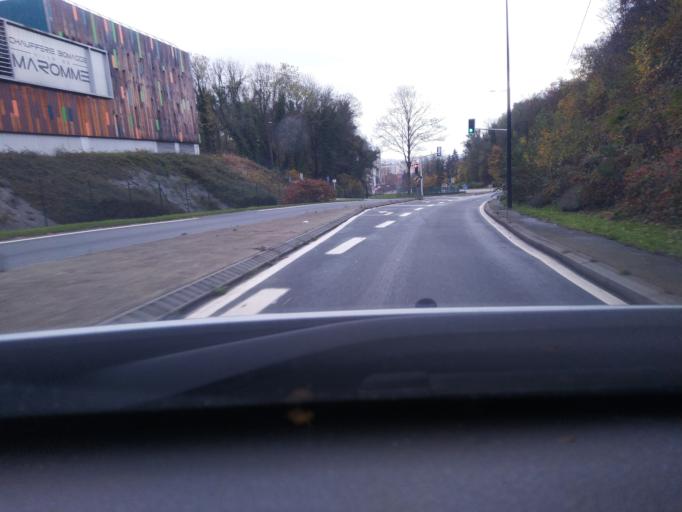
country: FR
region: Haute-Normandie
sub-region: Departement de la Seine-Maritime
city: Maromme
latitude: 49.4848
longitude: 1.0346
